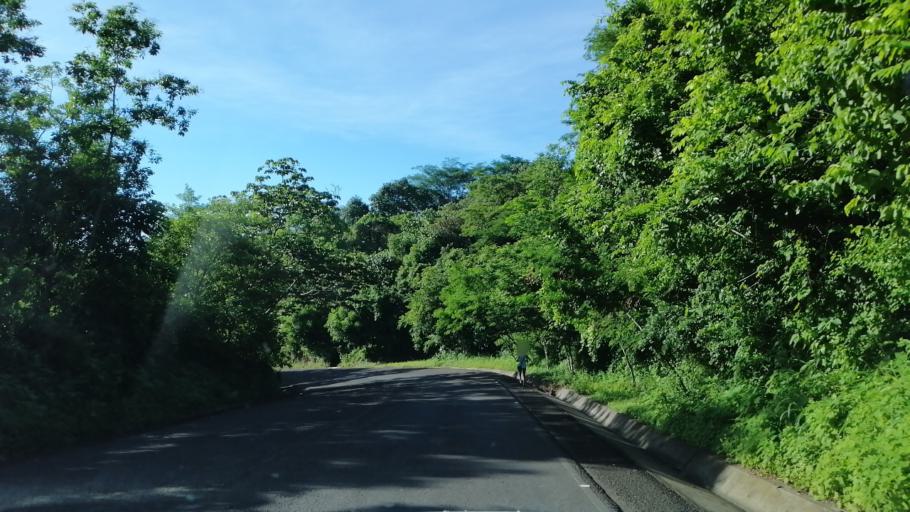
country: SV
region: Morazan
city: Cacaopera
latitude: 13.7907
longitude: -88.1300
